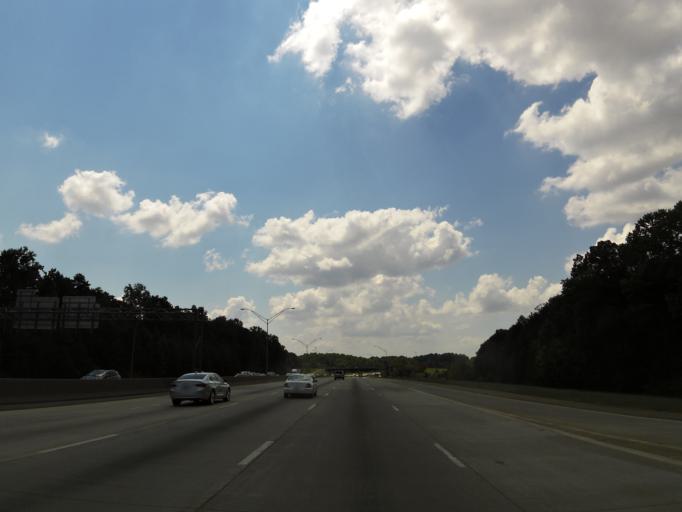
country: US
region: North Carolina
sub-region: Mecklenburg County
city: Charlotte
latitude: 35.2887
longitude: -80.7716
